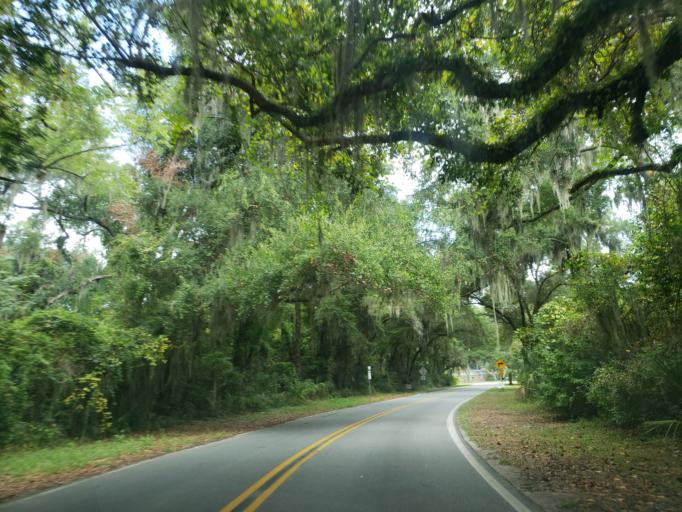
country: US
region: Georgia
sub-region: Chatham County
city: Wilmington Island
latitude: 31.9755
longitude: -80.9982
